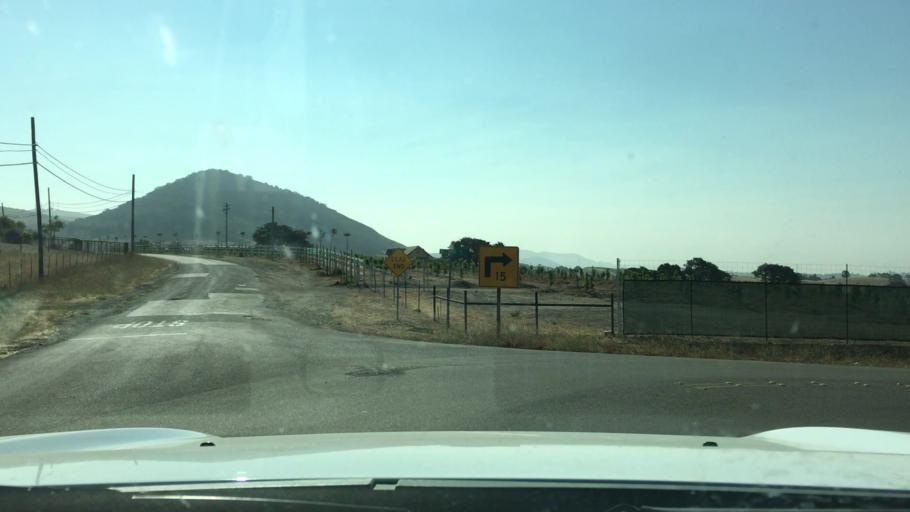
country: US
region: California
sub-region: San Luis Obispo County
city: Arroyo Grande
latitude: 35.1045
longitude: -120.5580
